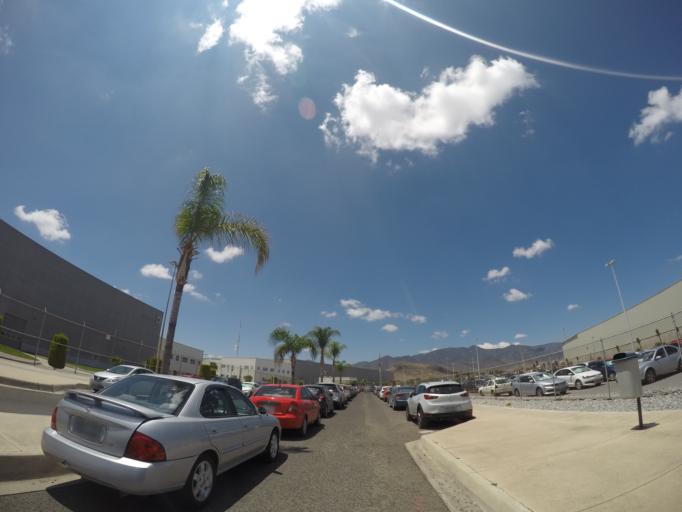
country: MX
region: San Luis Potosi
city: La Pila
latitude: 22.0374
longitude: -100.8914
